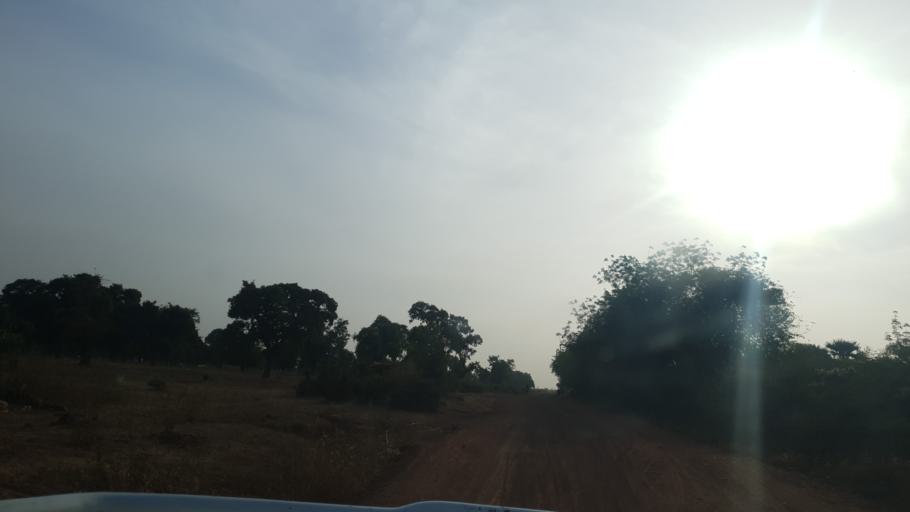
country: ML
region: Koulikoro
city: Dioila
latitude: 12.7705
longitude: -6.9312
